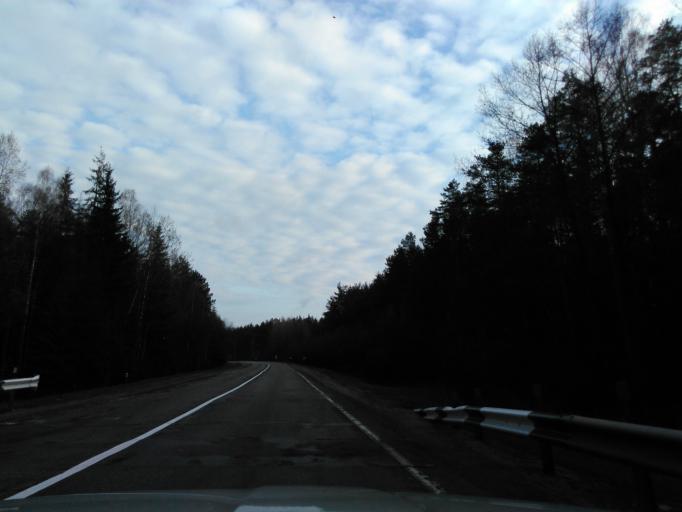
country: BY
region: Minsk
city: Plyeshchanitsy
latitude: 54.3854
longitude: 27.8729
